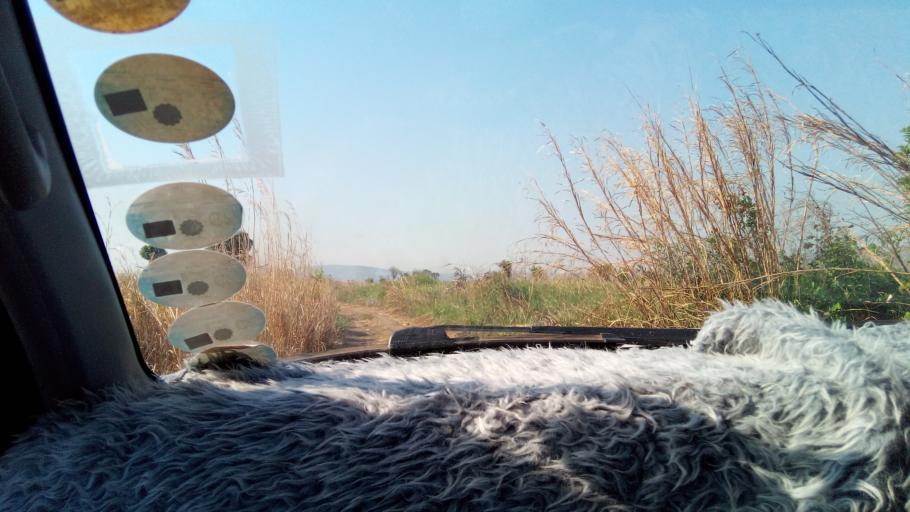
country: CD
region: Katanga
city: Kalemie
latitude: -5.9100
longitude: 29.1243
